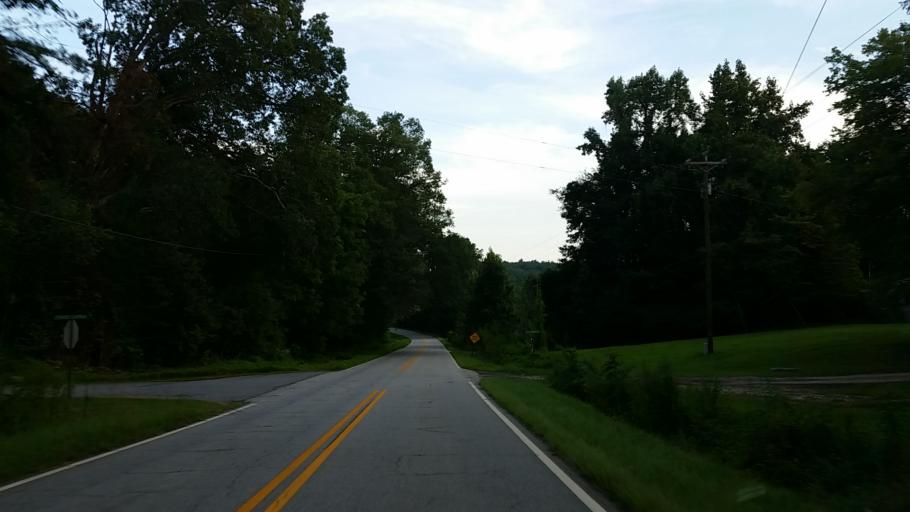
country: US
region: Georgia
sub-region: Lumpkin County
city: Dahlonega
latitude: 34.5911
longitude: -84.0360
